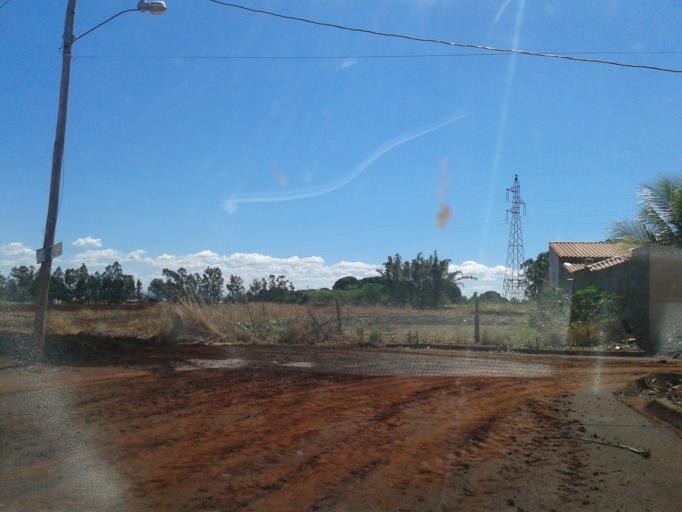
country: BR
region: Minas Gerais
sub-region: Centralina
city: Centralina
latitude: -18.5932
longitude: -49.2017
